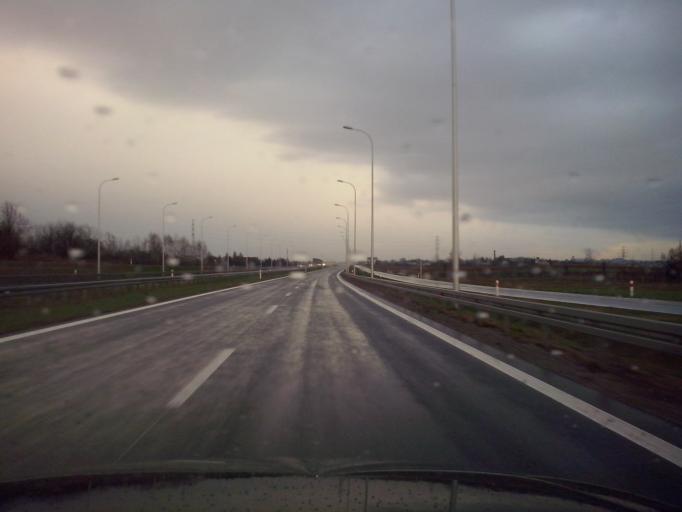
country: PL
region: Lublin Voivodeship
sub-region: Powiat lubelski
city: Jastkow
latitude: 51.2758
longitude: 22.4742
